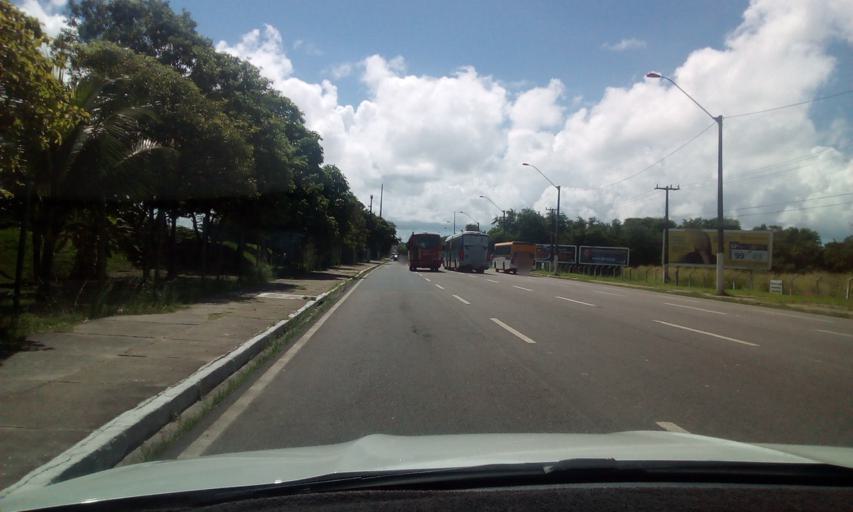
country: BR
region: Pernambuco
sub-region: Recife
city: Recife
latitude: -8.0335
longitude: -34.8670
